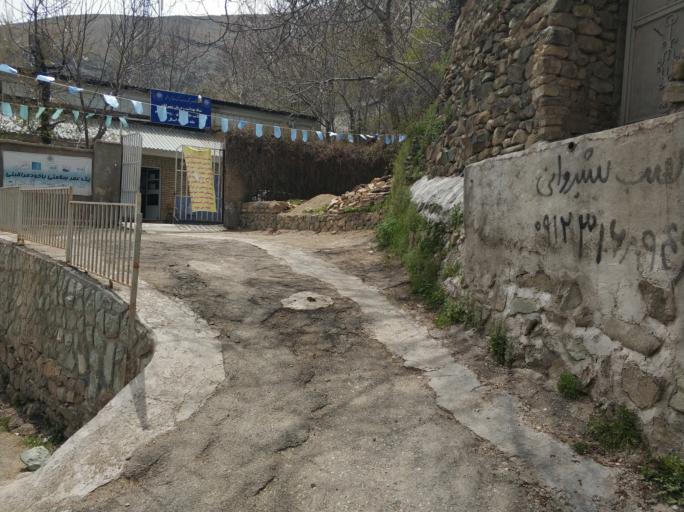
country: IR
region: Tehran
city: Tajrish
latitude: 35.9114
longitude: 51.4888
